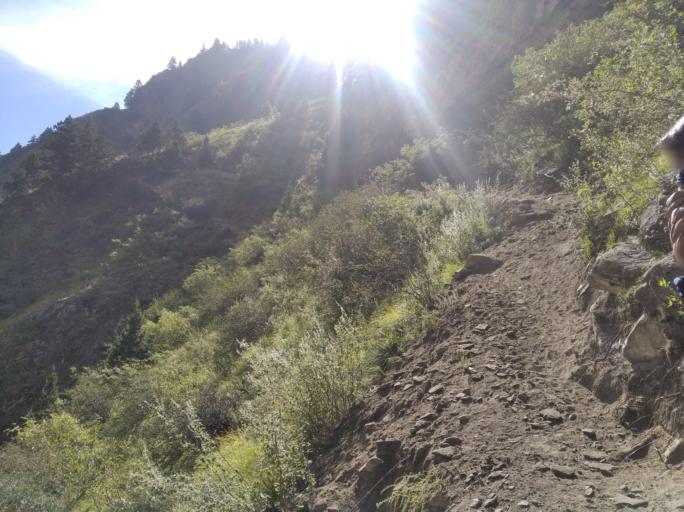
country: NP
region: Western Region
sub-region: Dhawalagiri Zone
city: Jomsom
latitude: 28.8966
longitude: 83.0494
